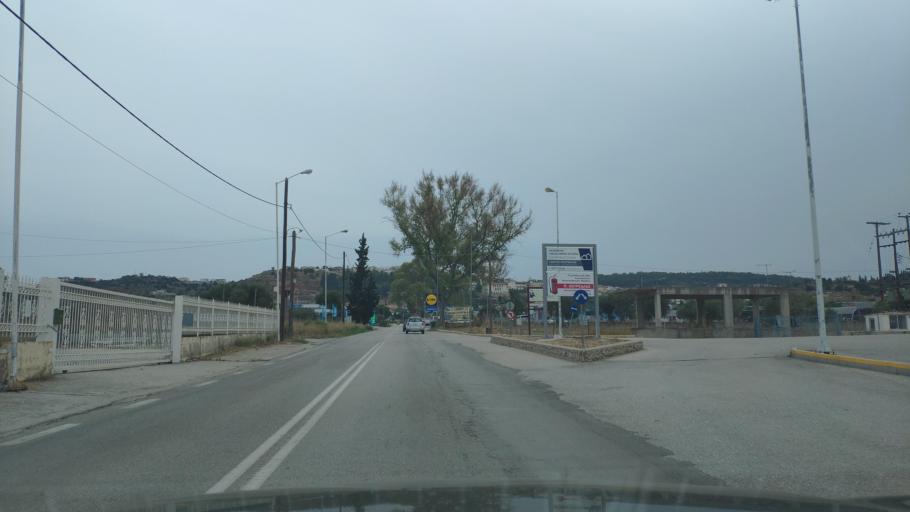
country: GR
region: Peloponnese
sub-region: Nomos Argolidos
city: Kranidi
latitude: 37.3912
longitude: 23.1576
